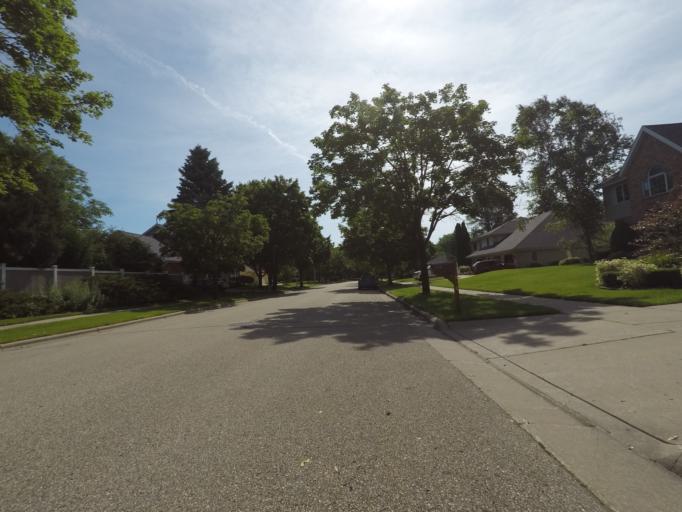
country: US
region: Wisconsin
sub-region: Dane County
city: Middleton
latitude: 43.0820
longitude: -89.4953
